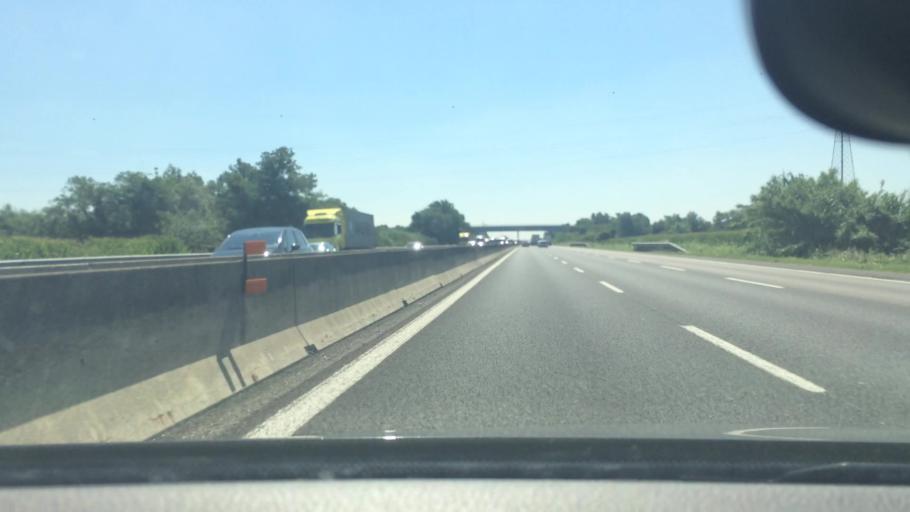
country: IT
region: Lombardy
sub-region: Provincia di Lodi
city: Salerano sul Lambro
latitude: 45.3096
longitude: 9.3941
